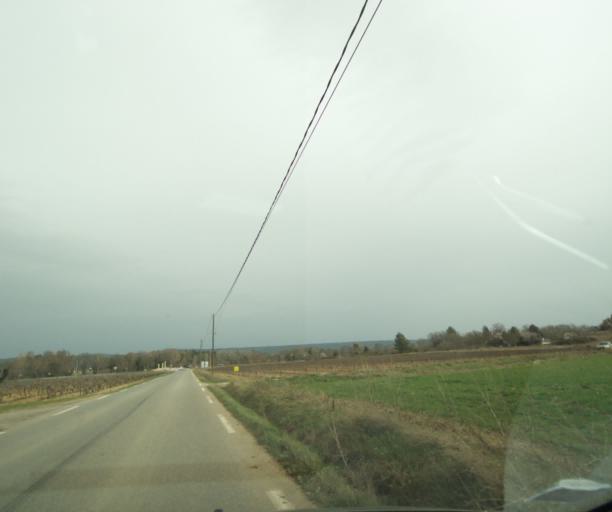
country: FR
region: Provence-Alpes-Cote d'Azur
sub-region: Departement du Var
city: Pourrieres
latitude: 43.4835
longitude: 5.7187
